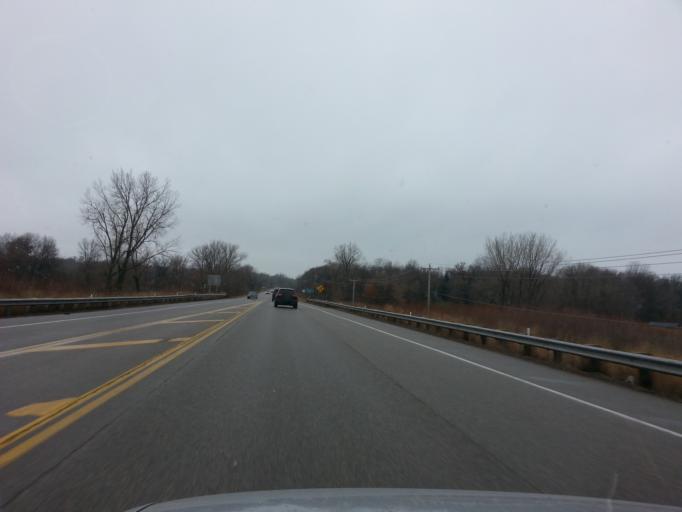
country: US
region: Minnesota
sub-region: Scott County
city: Prior Lake
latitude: 44.7397
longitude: -93.3817
